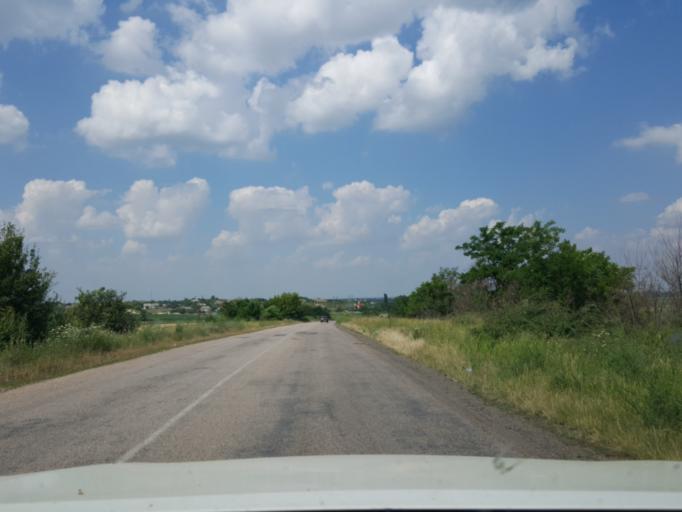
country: UA
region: Odessa
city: Starokozache
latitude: 46.3915
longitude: 30.0907
